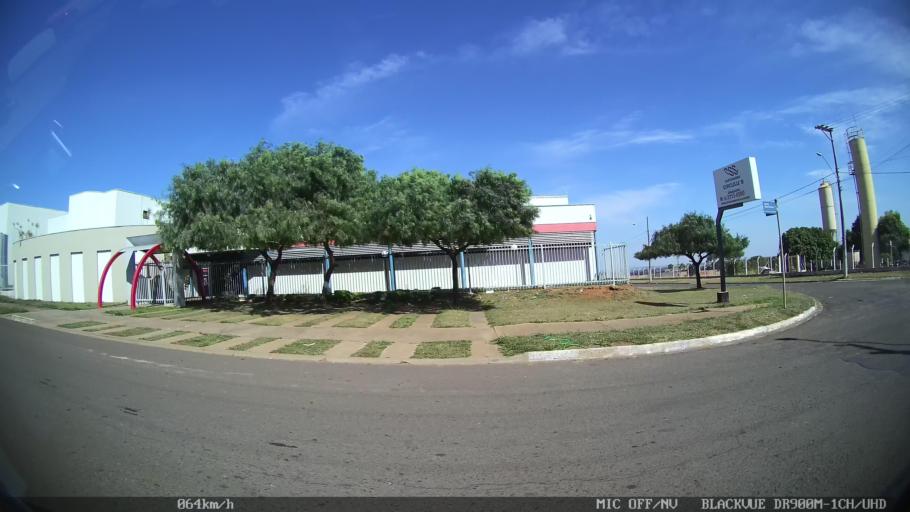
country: BR
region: Sao Paulo
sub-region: Franca
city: Franca
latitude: -20.5464
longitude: -47.4573
